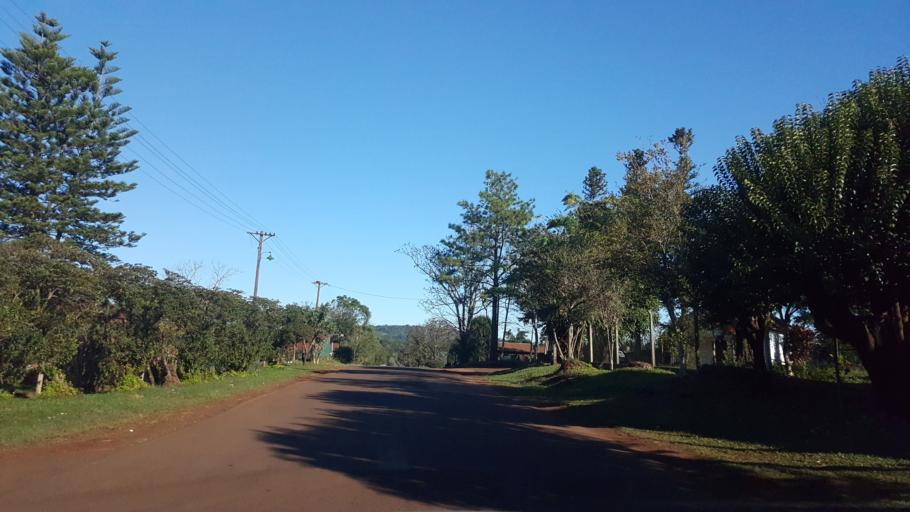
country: AR
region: Misiones
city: Jardin America
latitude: -27.0850
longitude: -55.2865
